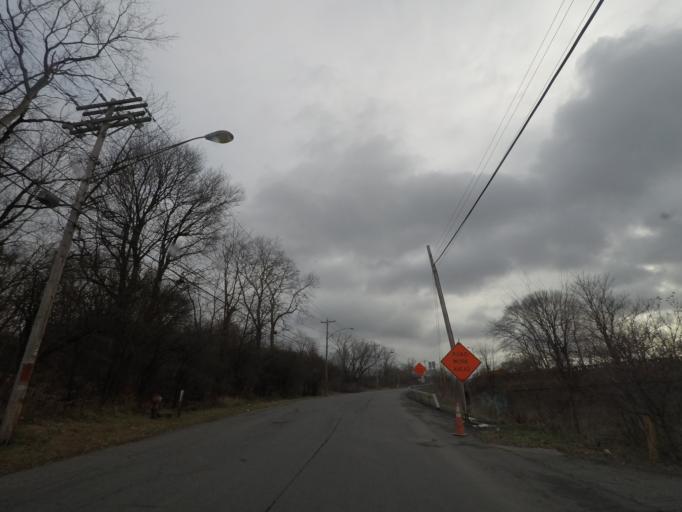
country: US
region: New York
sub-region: Rensselaer County
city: Rensselaer
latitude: 42.6312
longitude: -73.7432
